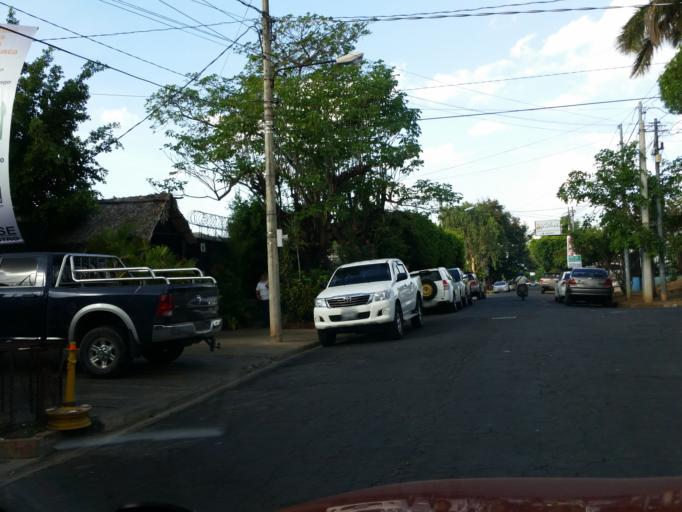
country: NI
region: Managua
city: Managua
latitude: 12.1238
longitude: -86.2606
